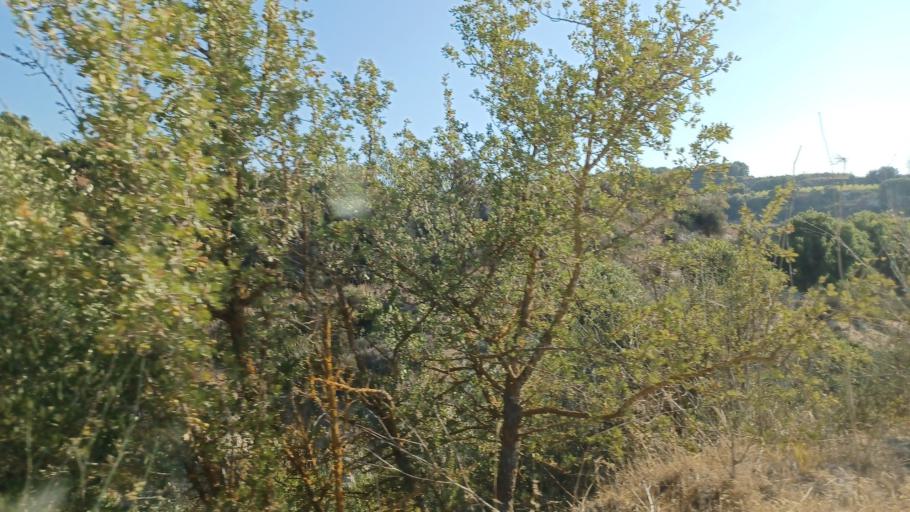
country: CY
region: Pafos
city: Mesogi
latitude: 34.8796
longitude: 32.5223
